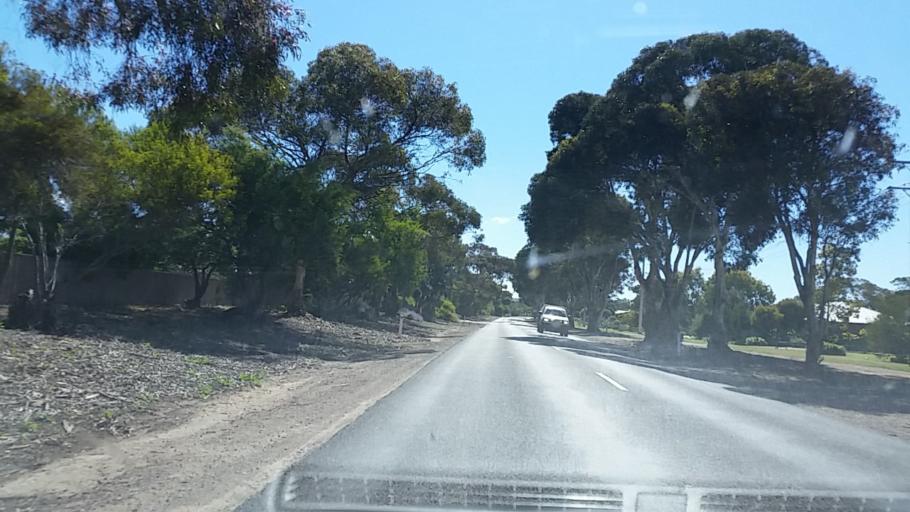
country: AU
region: South Australia
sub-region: Alexandrina
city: Strathalbyn
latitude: -35.2618
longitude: 138.9067
